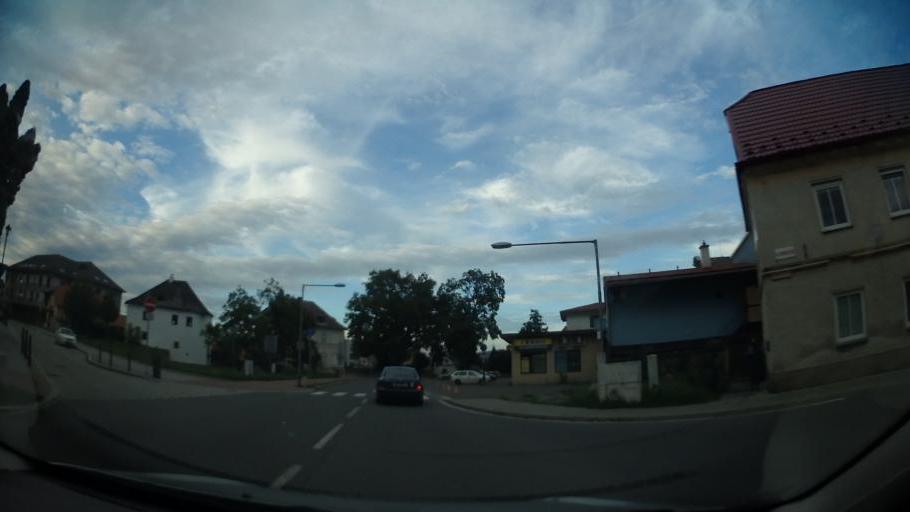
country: CZ
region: Olomoucky
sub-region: Okres Olomouc
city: Unicov
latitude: 49.7687
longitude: 17.1235
